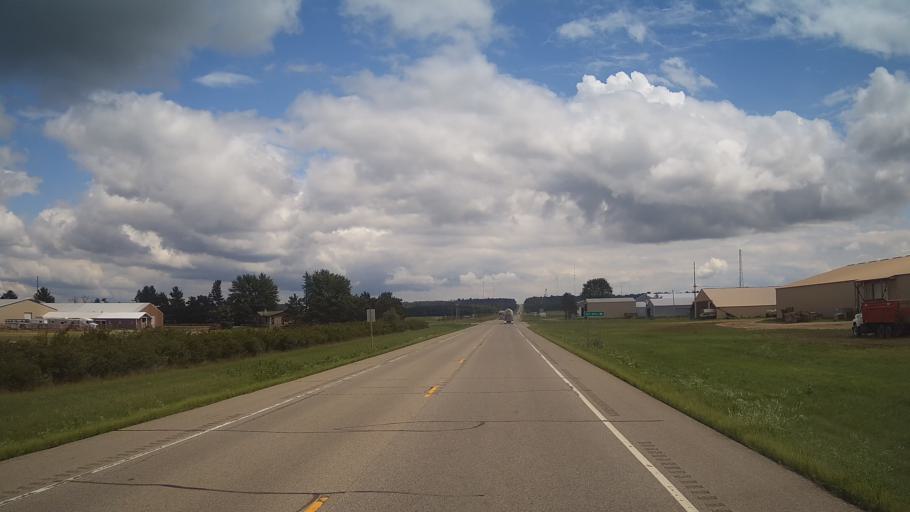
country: US
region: Wisconsin
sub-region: Marquette County
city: Westfield
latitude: 44.0221
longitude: -89.6012
